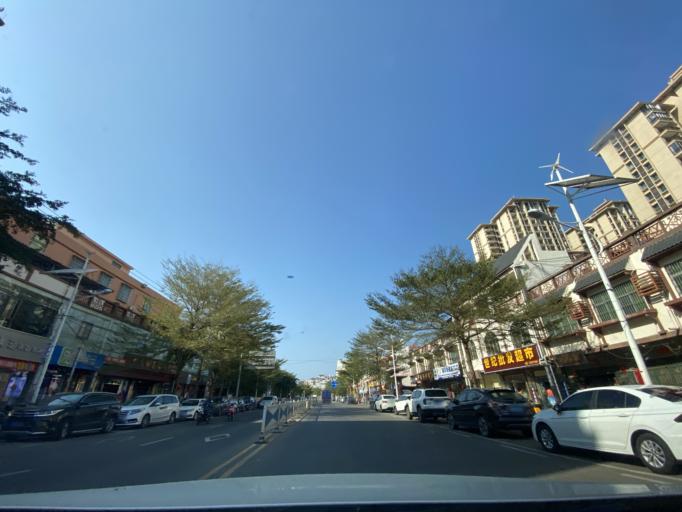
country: CN
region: Hainan
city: Yingzhou
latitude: 18.4254
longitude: 109.8550
